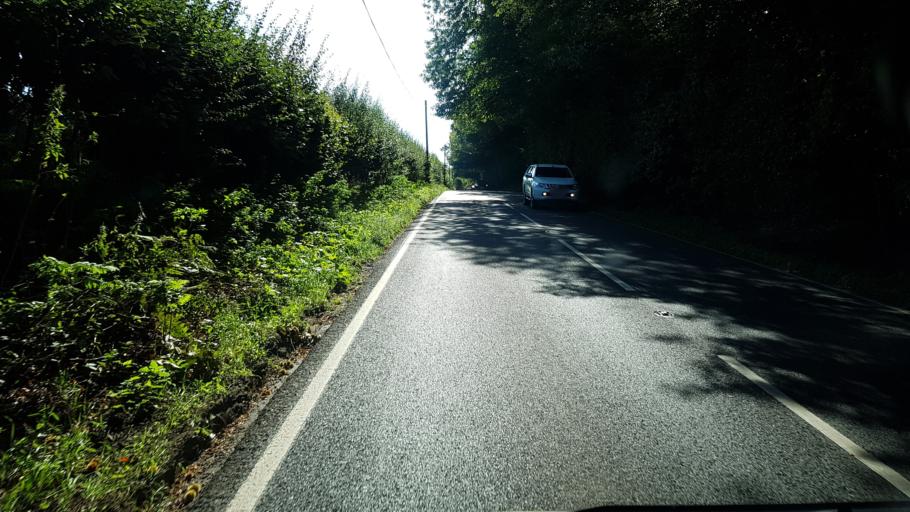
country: GB
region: England
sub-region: Kent
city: Borough Green
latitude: 51.2816
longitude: 0.3513
